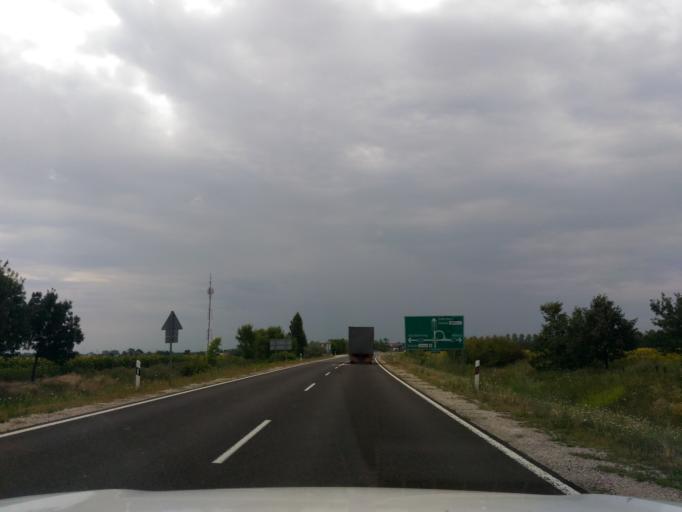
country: HU
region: Jasz-Nagykun-Szolnok
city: Zagyvarekas
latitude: 47.1867
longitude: 20.0957
